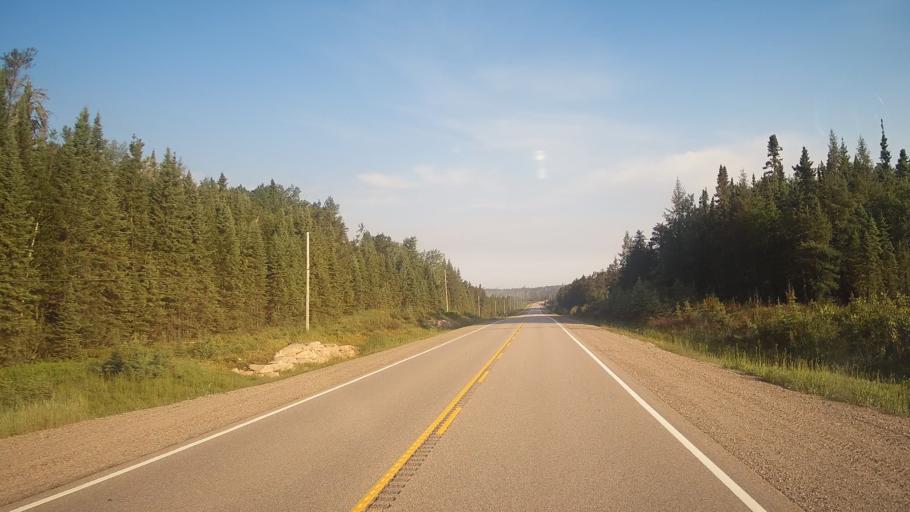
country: CA
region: Ontario
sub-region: Rainy River District
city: Atikokan
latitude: 49.3812
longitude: -91.5870
